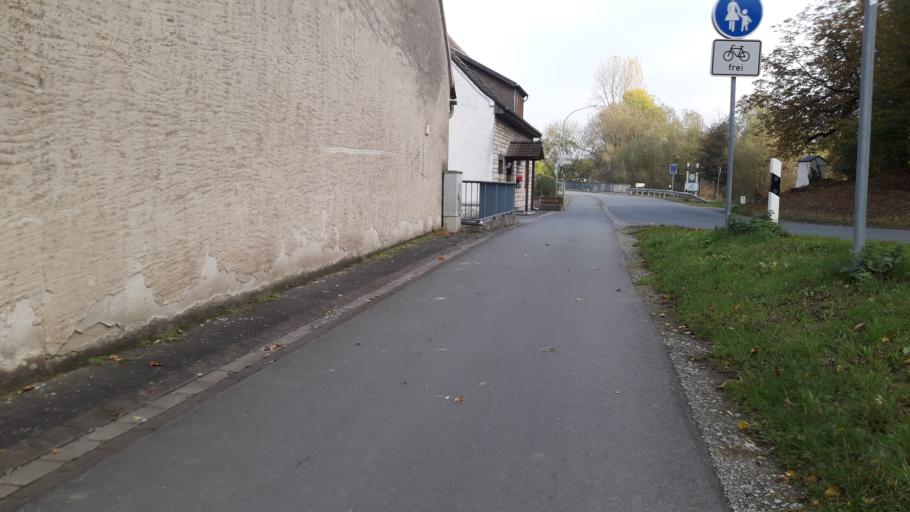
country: DE
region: North Rhine-Westphalia
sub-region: Regierungsbezirk Detmold
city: Paderborn
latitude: 51.6721
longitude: 8.7158
